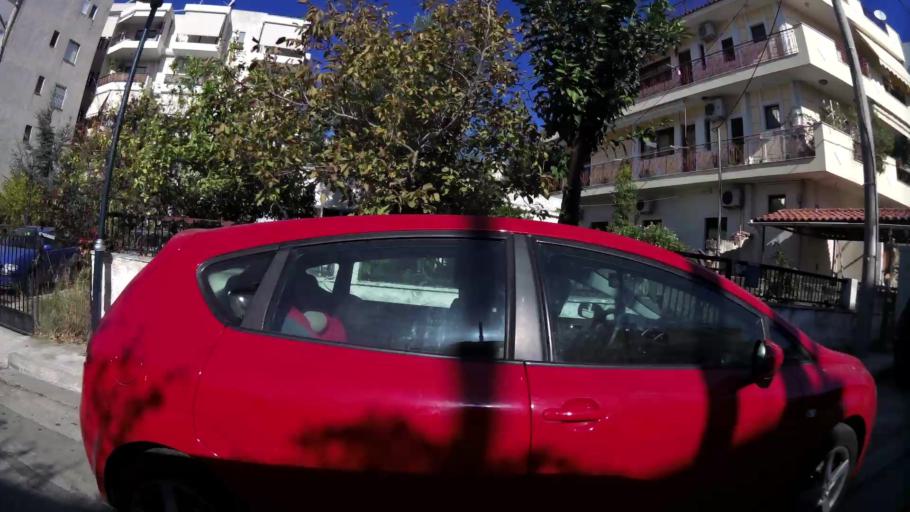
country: GR
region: Attica
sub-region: Nomarchia Athinas
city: Metamorfosi
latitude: 38.0656
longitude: 23.7723
